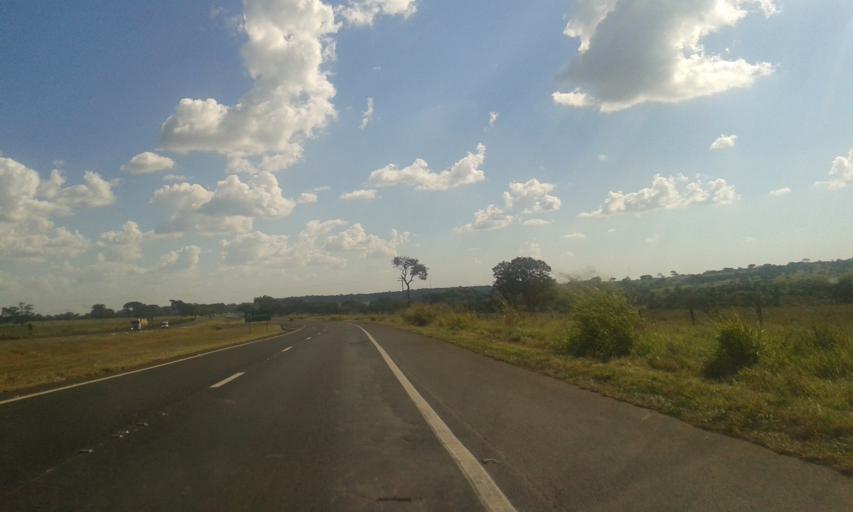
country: BR
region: Minas Gerais
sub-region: Monte Alegre De Minas
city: Monte Alegre de Minas
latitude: -18.8908
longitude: -48.6358
